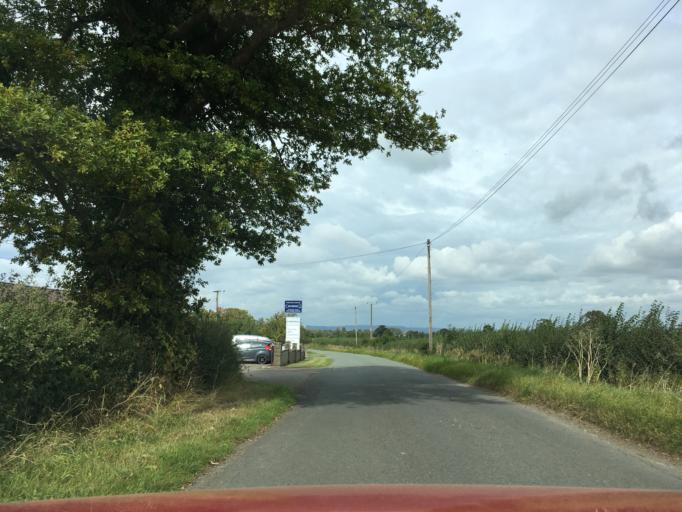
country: GB
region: England
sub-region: South Gloucestershire
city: Thornbury
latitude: 51.6147
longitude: -2.5547
